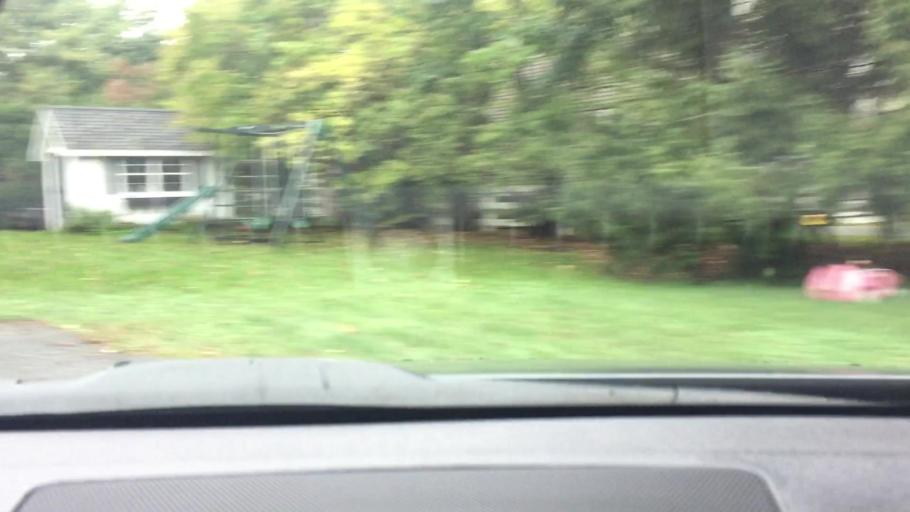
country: US
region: Massachusetts
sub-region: Norfolk County
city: Needham
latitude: 42.2870
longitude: -71.2292
